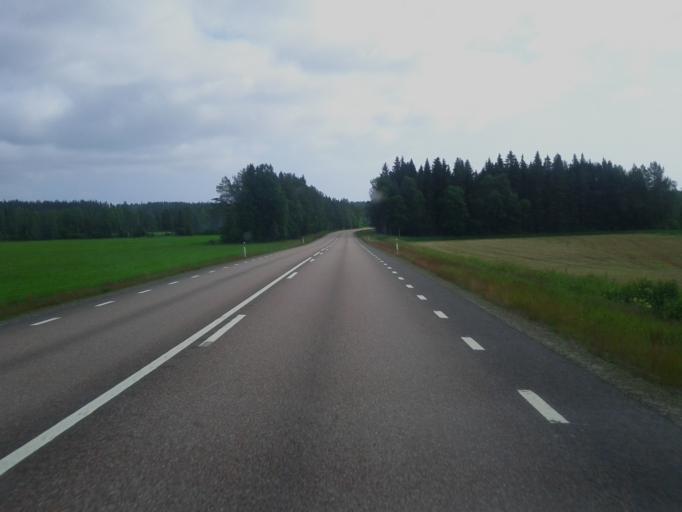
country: SE
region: Vaesterbotten
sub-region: Skelleftea Kommun
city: Burea
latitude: 64.3341
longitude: 21.2433
